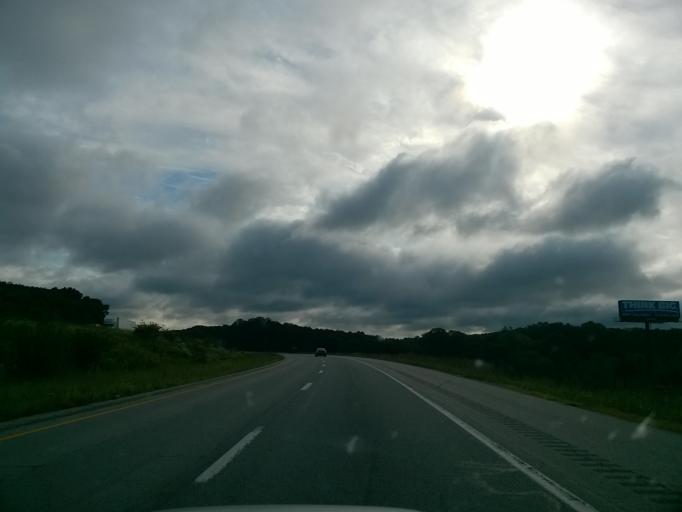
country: US
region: Indiana
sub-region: Crawford County
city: English
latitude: 38.2291
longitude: -86.5697
